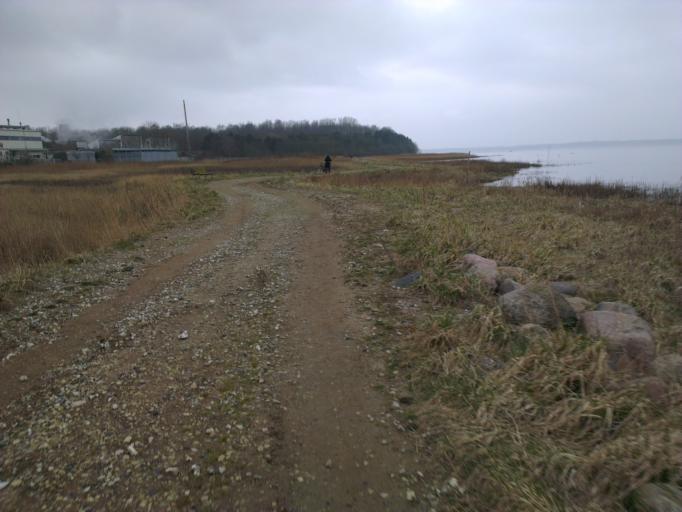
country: DK
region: Capital Region
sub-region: Frederikssund Kommune
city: Frederikssund
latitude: 55.8581
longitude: 12.0577
